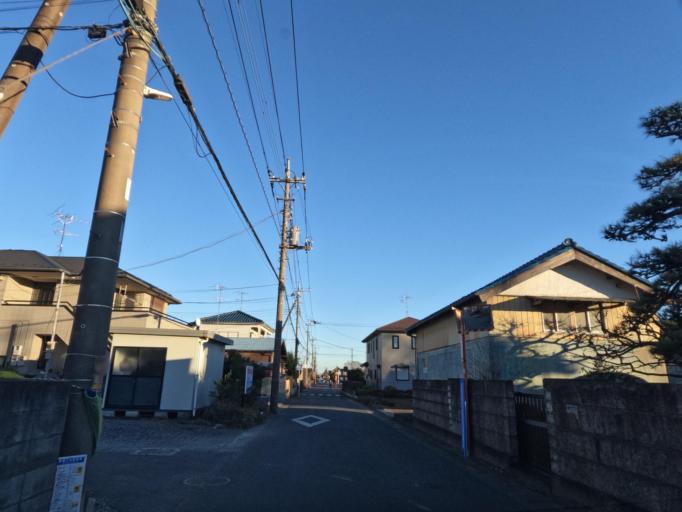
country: JP
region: Saitama
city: Iwatsuki
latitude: 35.9619
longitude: 139.6822
